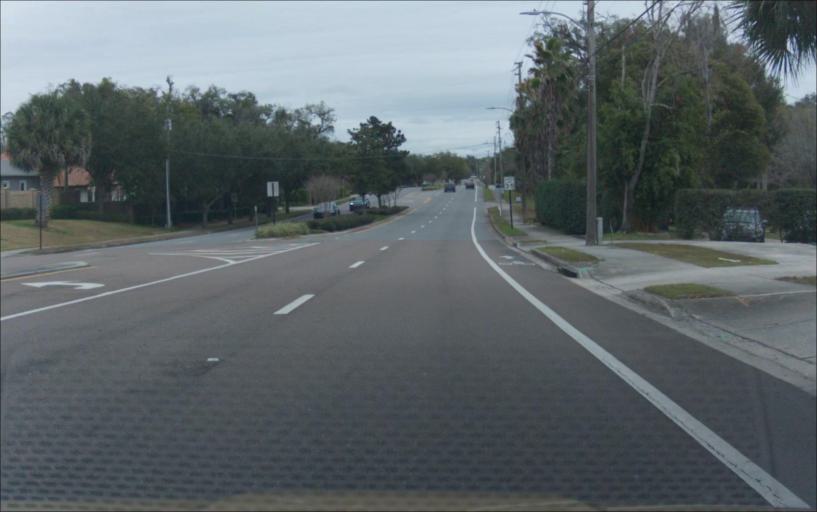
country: US
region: Florida
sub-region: Orange County
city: Maitland
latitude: 28.6258
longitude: -81.3410
